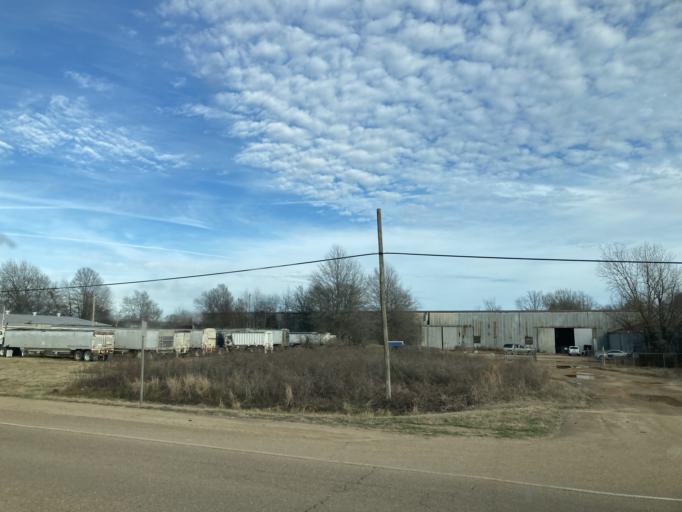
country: US
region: Mississippi
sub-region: Humphreys County
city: Belzoni
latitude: 33.1661
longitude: -90.4989
